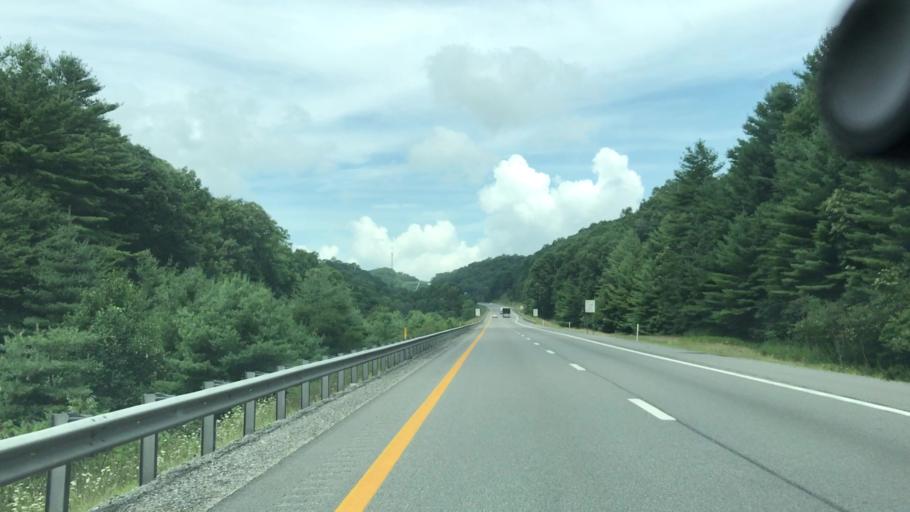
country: US
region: West Virginia
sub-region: Raleigh County
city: Beaver
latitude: 37.7190
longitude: -81.1651
